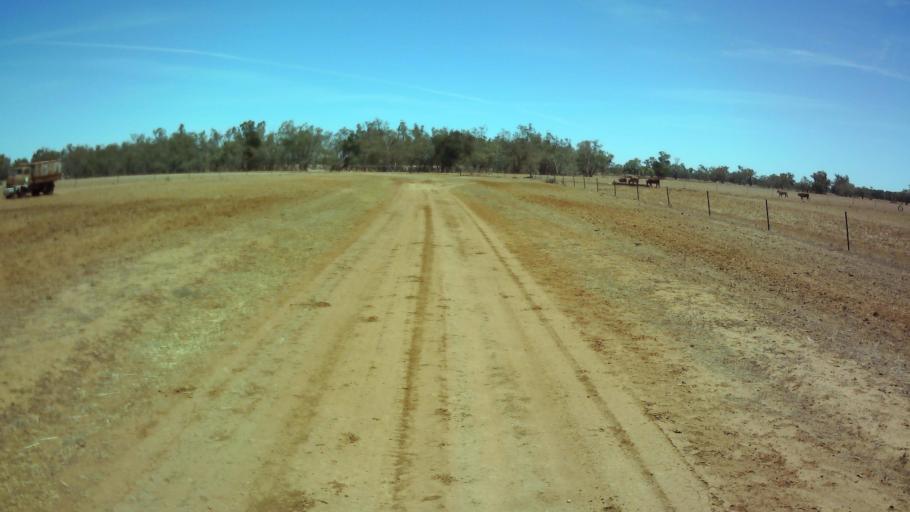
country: AU
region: New South Wales
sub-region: Bland
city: West Wyalong
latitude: -33.8306
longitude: 147.6365
